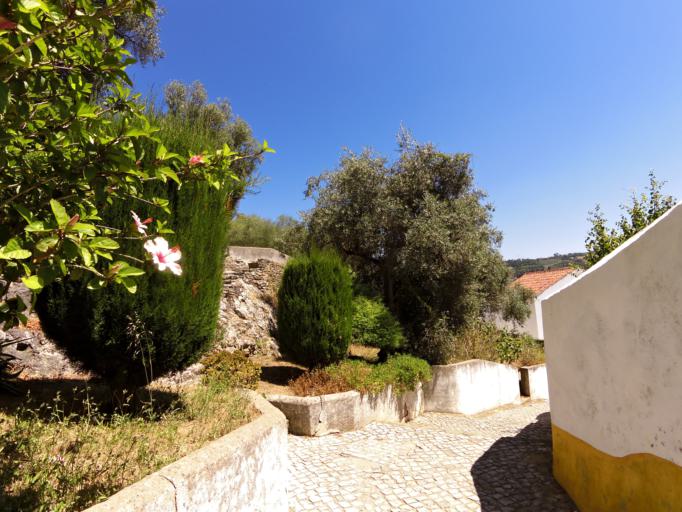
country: PT
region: Leiria
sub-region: Obidos
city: Obidos
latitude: 39.3627
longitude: -9.1561
